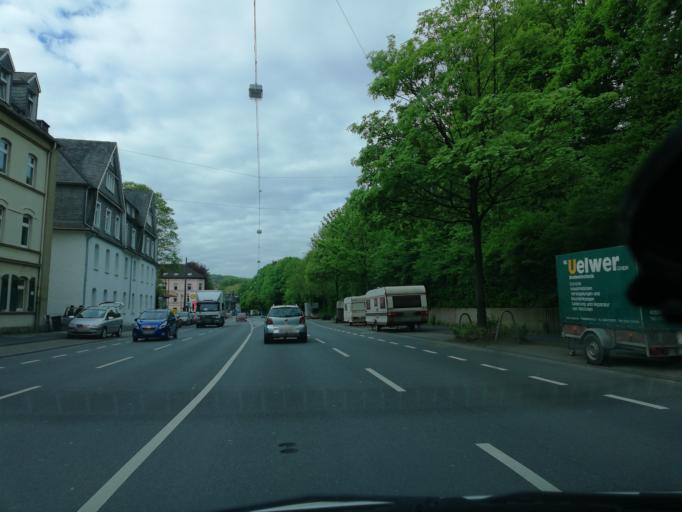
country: DE
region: North Rhine-Westphalia
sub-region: Regierungsbezirk Arnsberg
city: Schwelm
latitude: 51.2801
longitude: 7.2386
